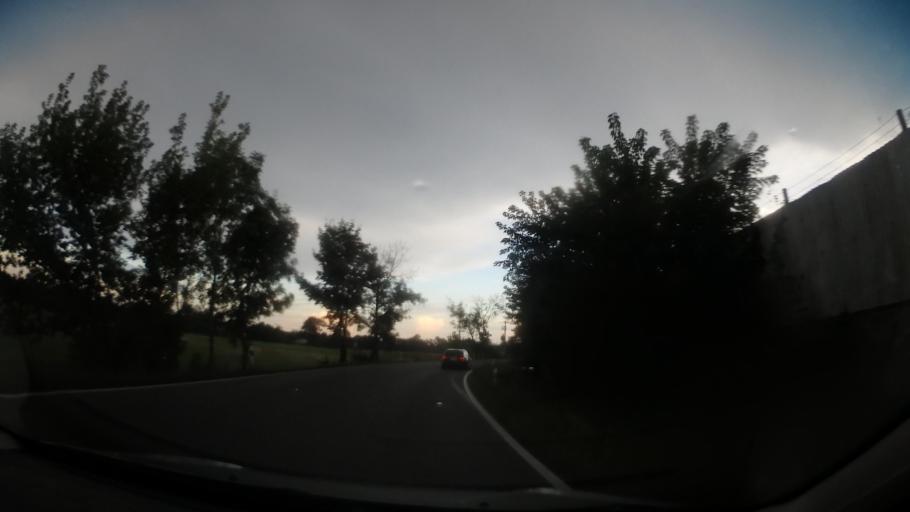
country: CZ
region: Olomoucky
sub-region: Okres Olomouc
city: Olomouc
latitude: 49.6204
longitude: 17.2506
